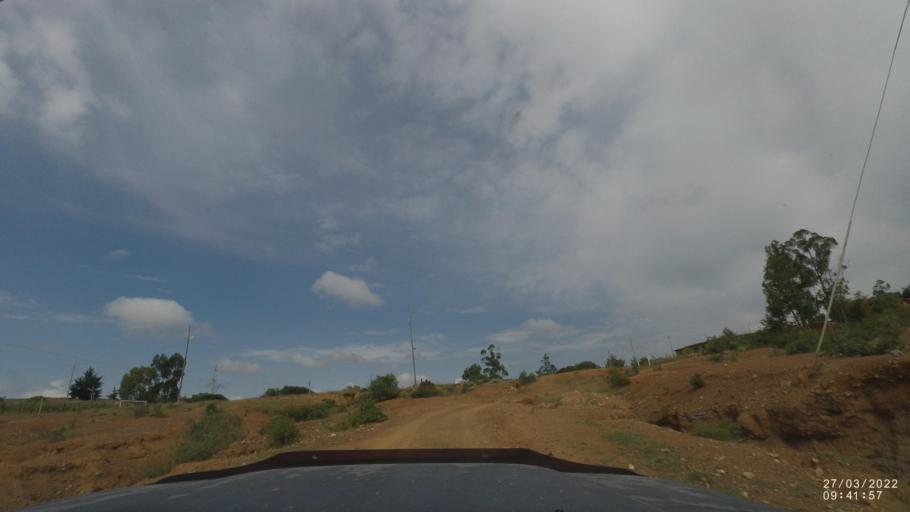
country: BO
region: Cochabamba
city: Cliza
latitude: -17.7520
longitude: -65.9014
